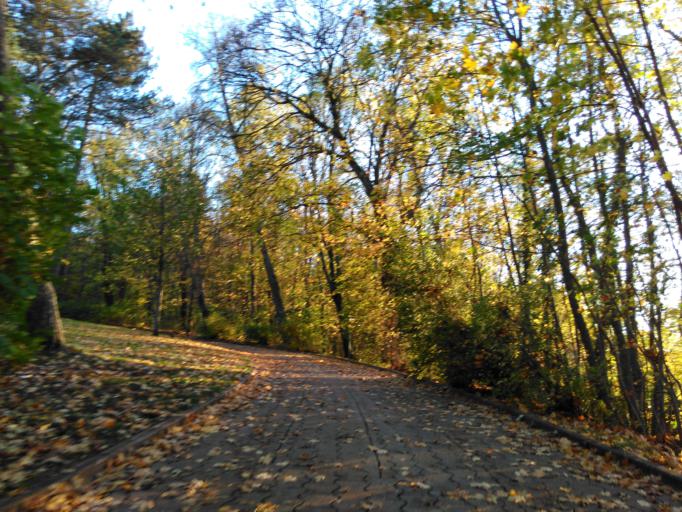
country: LU
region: Luxembourg
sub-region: Canton d'Esch-sur-Alzette
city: Esch-sur-Alzette
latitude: 49.4910
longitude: 5.9843
